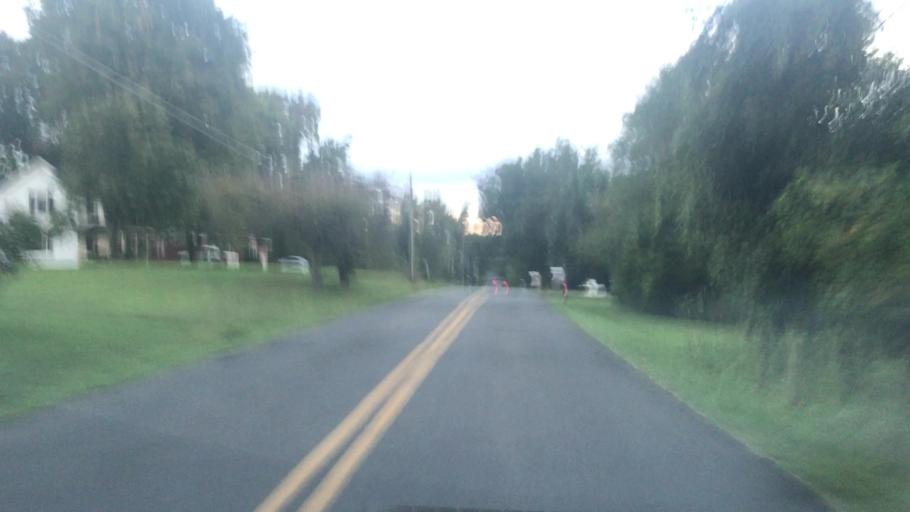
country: US
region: Virginia
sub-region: Prince William County
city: Nokesville
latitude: 38.6976
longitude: -77.6675
